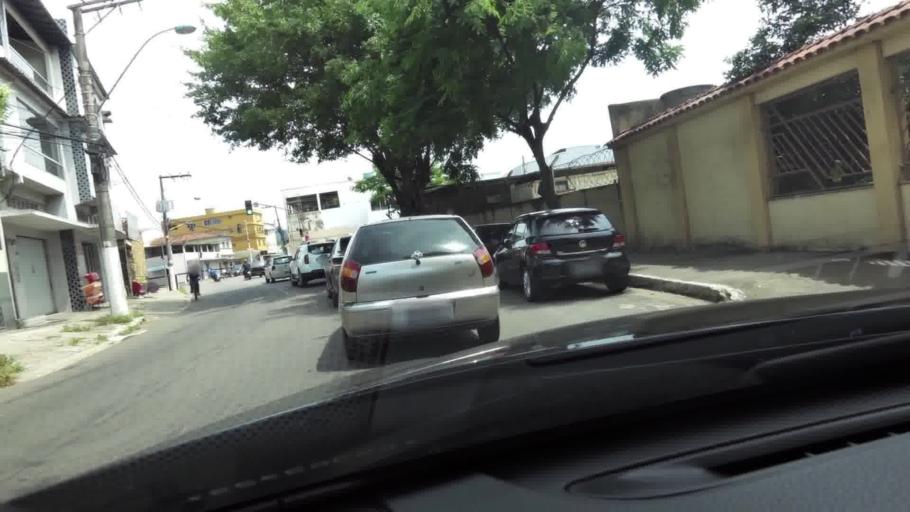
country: BR
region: Espirito Santo
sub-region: Vila Velha
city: Vila Velha
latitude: -20.3413
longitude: -40.3049
